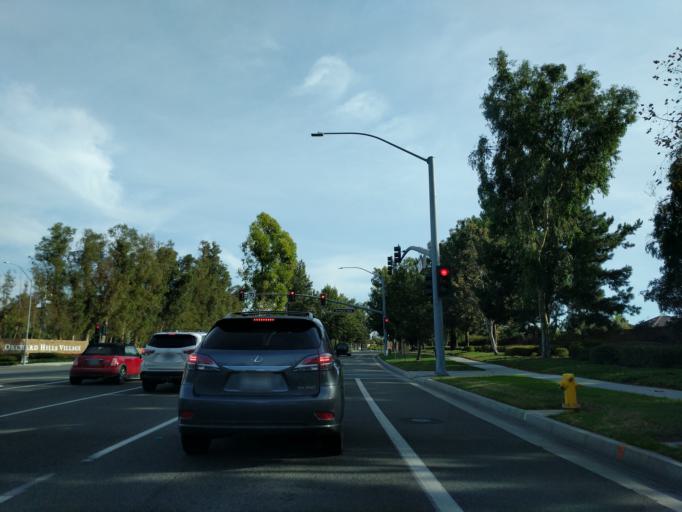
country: US
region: California
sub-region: Orange County
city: North Tustin
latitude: 33.7278
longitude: -117.7489
